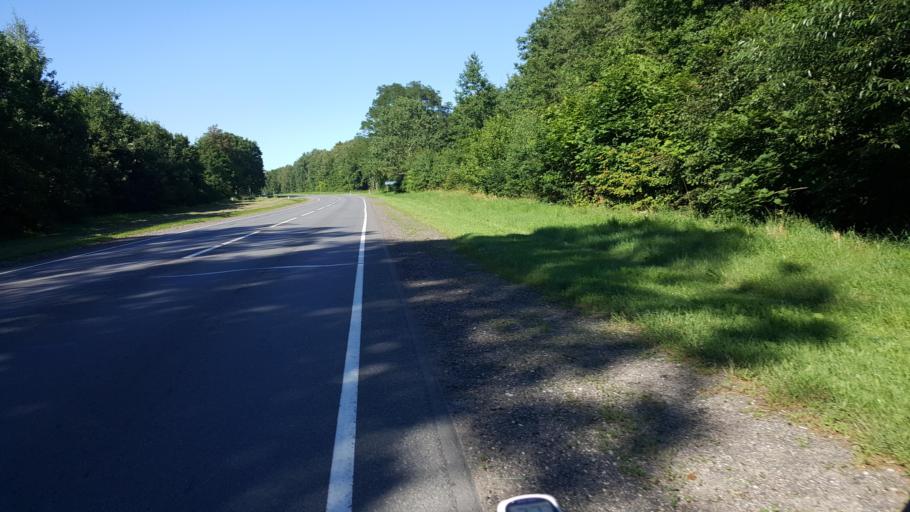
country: BY
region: Brest
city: Charnawchytsy
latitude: 52.2636
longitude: 23.7641
